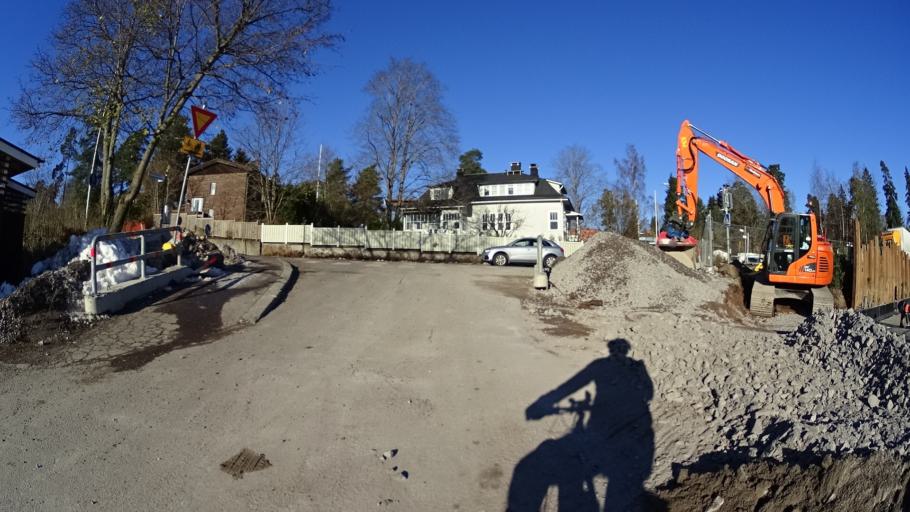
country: FI
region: Uusimaa
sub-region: Helsinki
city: Kauniainen
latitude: 60.2113
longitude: 24.7182
